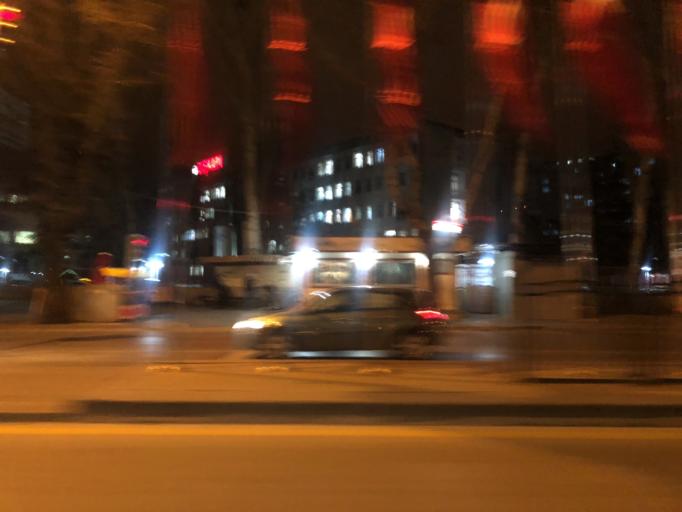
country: TR
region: Ankara
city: Ankara
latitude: 39.9552
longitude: 32.8613
